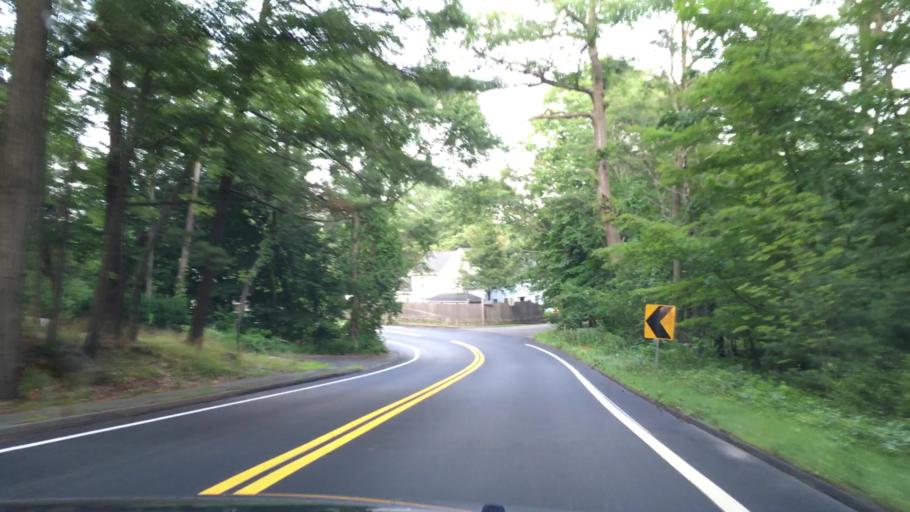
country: US
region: Massachusetts
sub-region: Essex County
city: Essex
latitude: 42.5789
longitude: -70.7435
